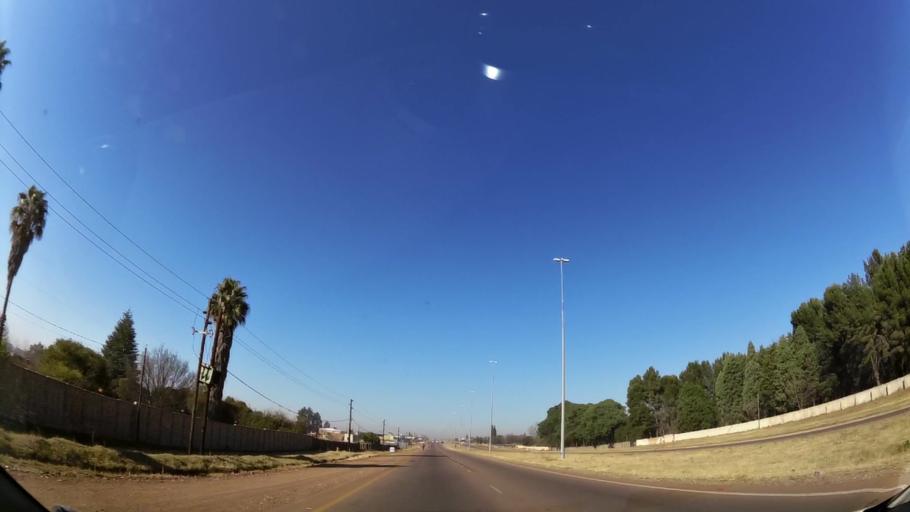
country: ZA
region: Gauteng
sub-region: City of Tshwane Metropolitan Municipality
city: Centurion
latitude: -25.8534
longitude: 28.1085
